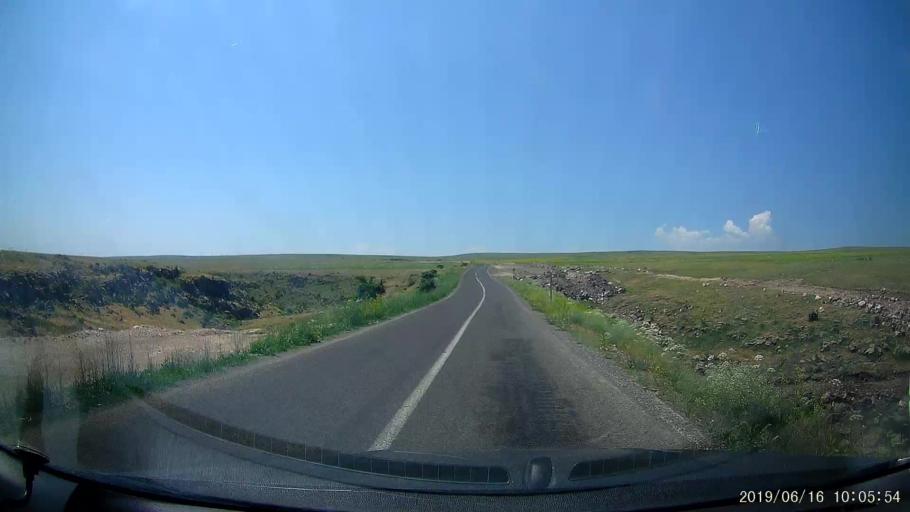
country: TR
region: Kars
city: Digor
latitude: 40.2637
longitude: 43.5398
